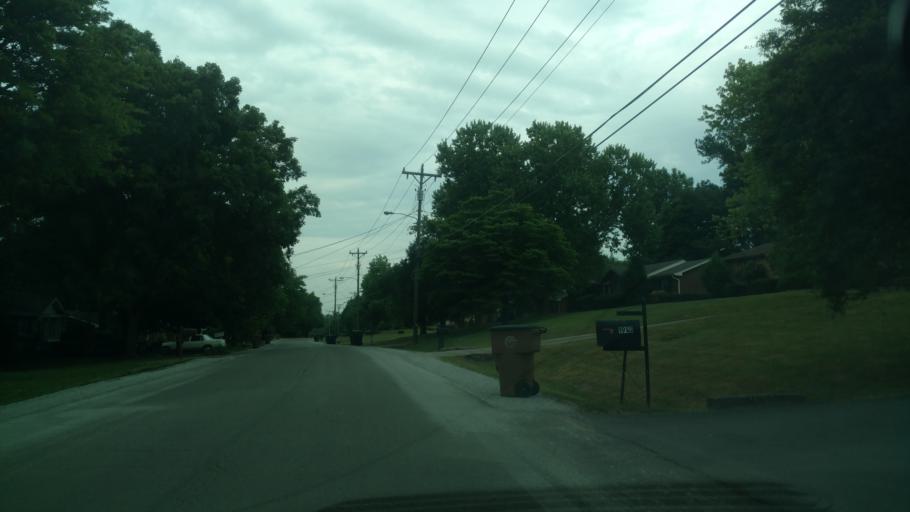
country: US
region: Tennessee
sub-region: Davidson County
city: Nashville
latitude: 36.1994
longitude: -86.7145
